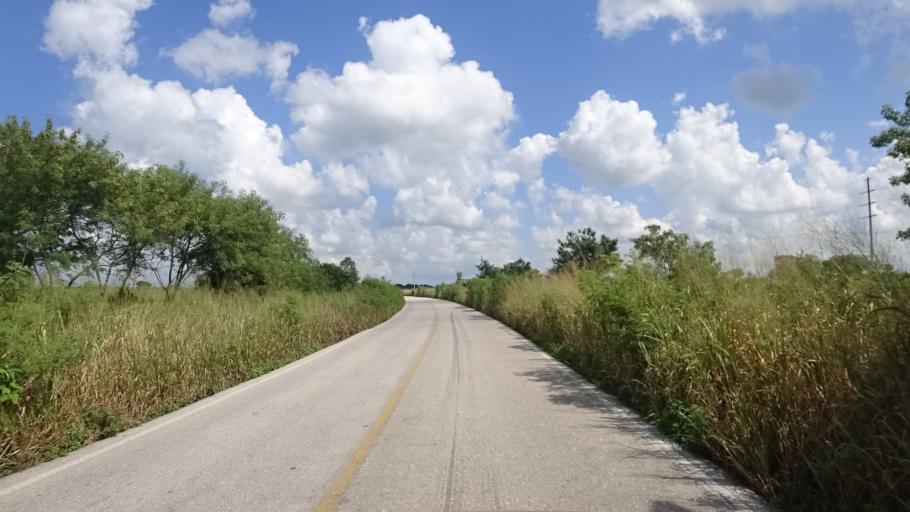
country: MX
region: Yucatan
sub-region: Panaba
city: Loche
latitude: 21.3624
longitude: -88.1444
